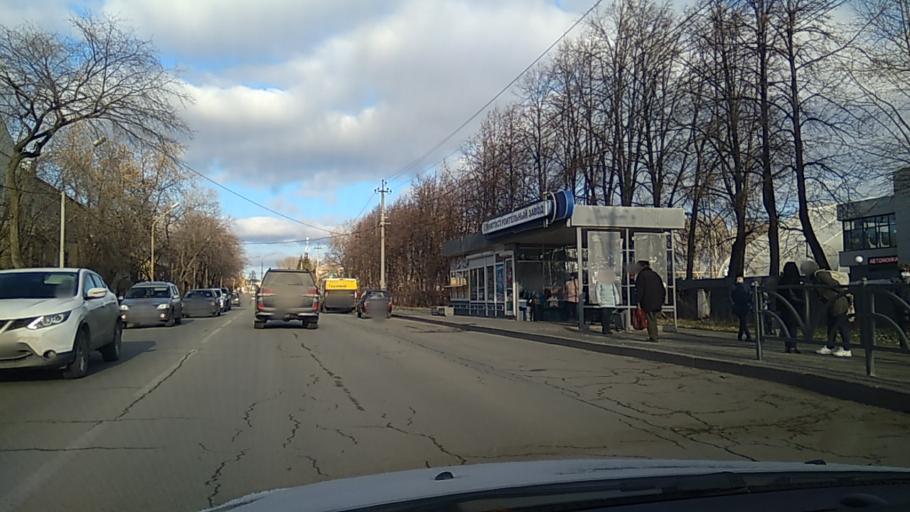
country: RU
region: Sverdlovsk
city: Sovkhoznyy
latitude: 56.7536
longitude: 60.6233
